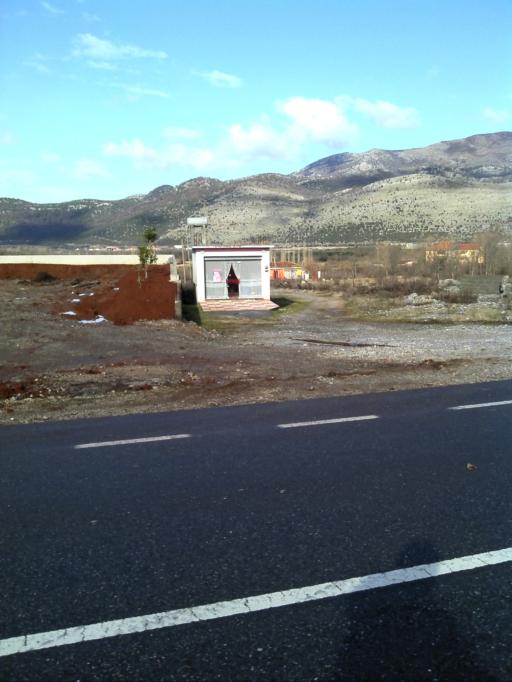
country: AL
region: Shkoder
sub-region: Rrethi i Malesia e Madhe
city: Hot
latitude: 42.3266
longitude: 19.4393
